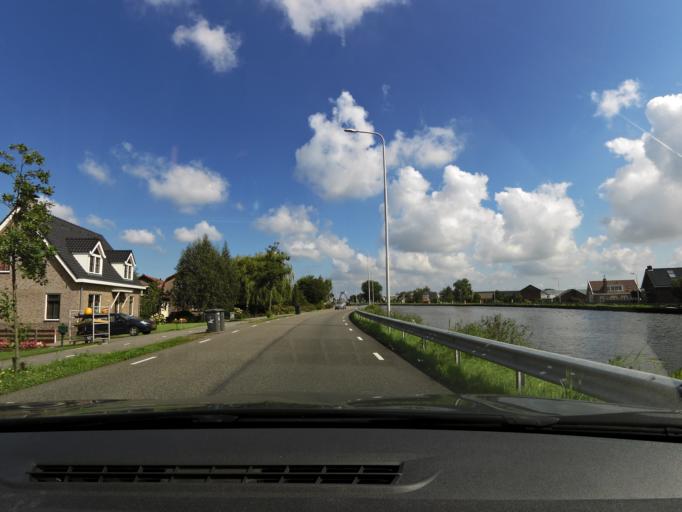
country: NL
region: South Holland
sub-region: Gemeente Nieuwkoop
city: Nieuwkoop
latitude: 52.1810
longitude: 4.7237
